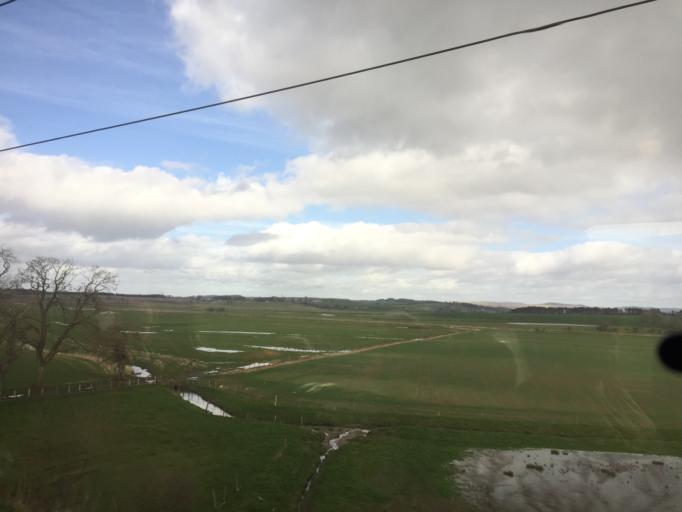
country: GB
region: Scotland
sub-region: South Lanarkshire
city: Carnwath
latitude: 55.6679
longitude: -3.6368
